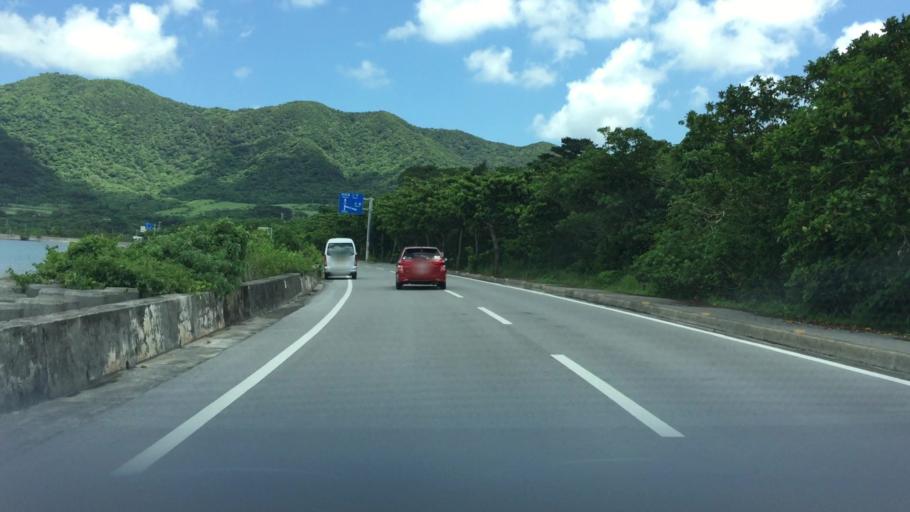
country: JP
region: Okinawa
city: Ishigaki
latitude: 24.4060
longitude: 124.1435
